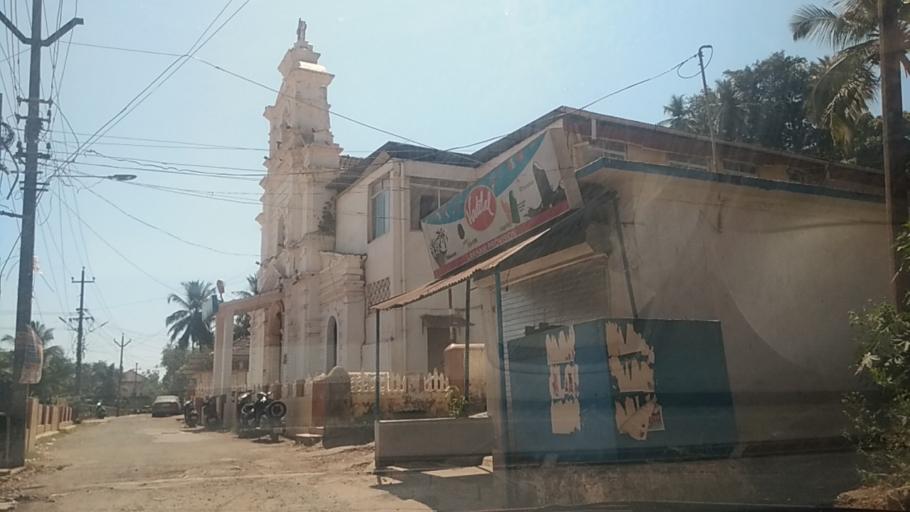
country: IN
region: Goa
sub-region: South Goa
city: Vasco Da Gama
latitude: 15.3979
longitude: 73.8040
